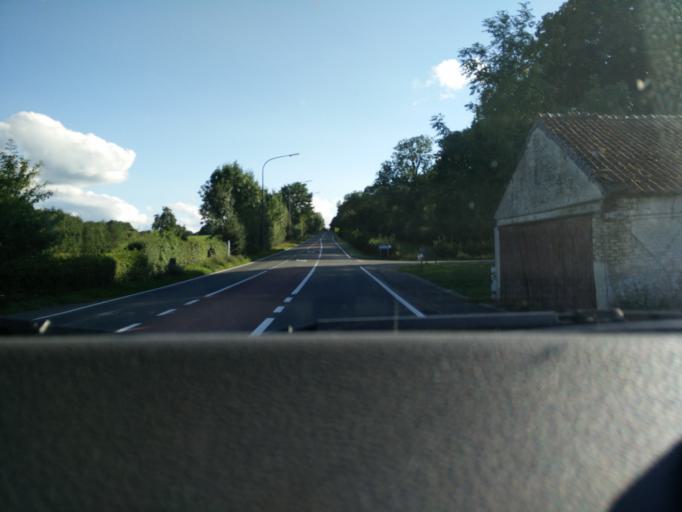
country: BE
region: Wallonia
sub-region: Province du Hainaut
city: Beaumont
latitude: 50.1909
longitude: 4.2203
